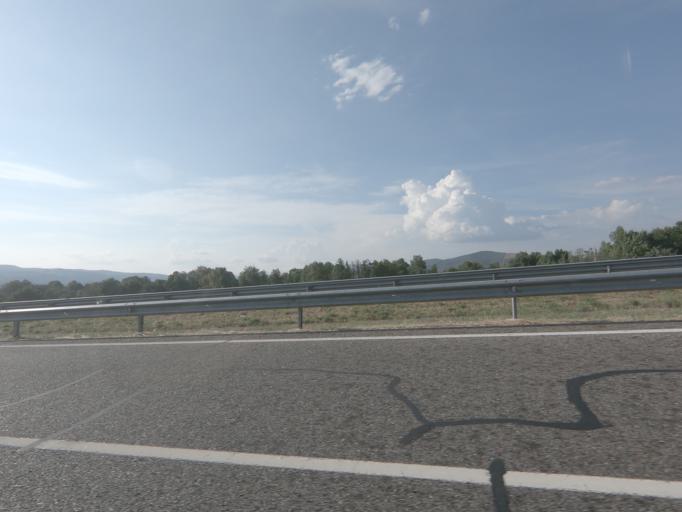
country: ES
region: Galicia
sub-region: Provincia de Ourense
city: Verin
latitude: 41.9227
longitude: -7.4694
